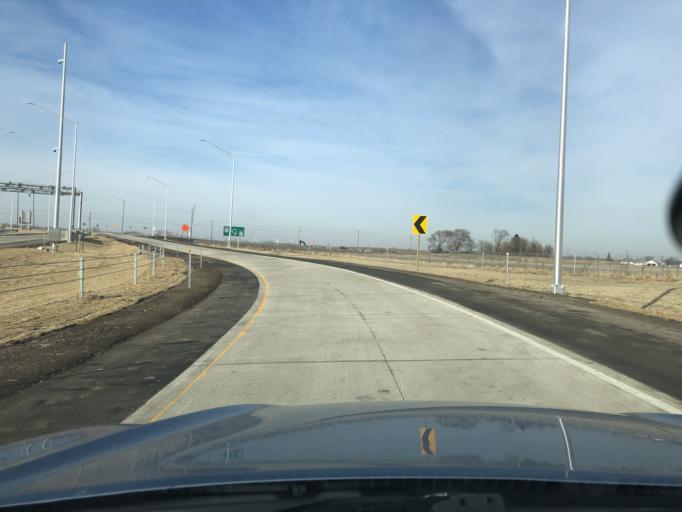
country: US
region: Illinois
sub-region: McHenry County
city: Marengo
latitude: 42.1787
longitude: -88.6148
